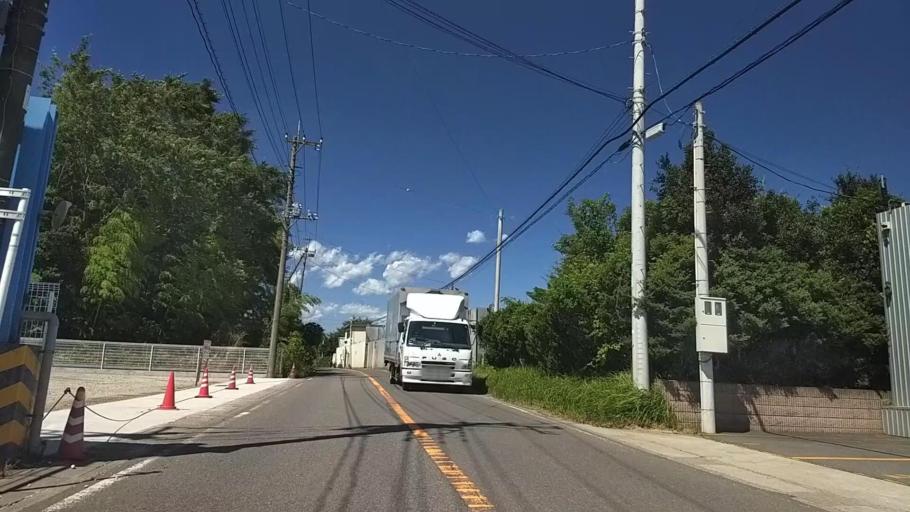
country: JP
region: Kanagawa
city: Zama
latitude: 35.5360
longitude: 139.3483
